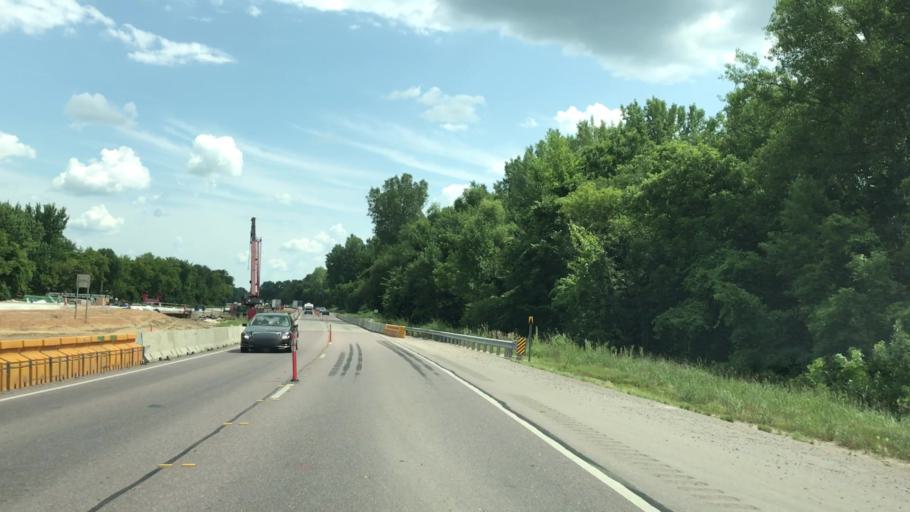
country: US
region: Minnesota
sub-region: Nicollet County
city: Saint Peter
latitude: 44.3666
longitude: -93.9644
